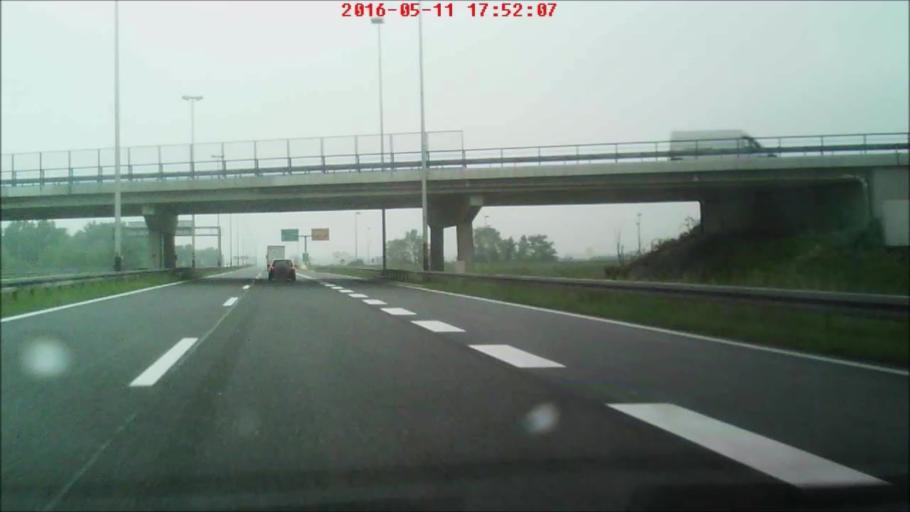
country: HR
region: Zagrebacka
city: Zapresic
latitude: 45.8551
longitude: 15.8279
